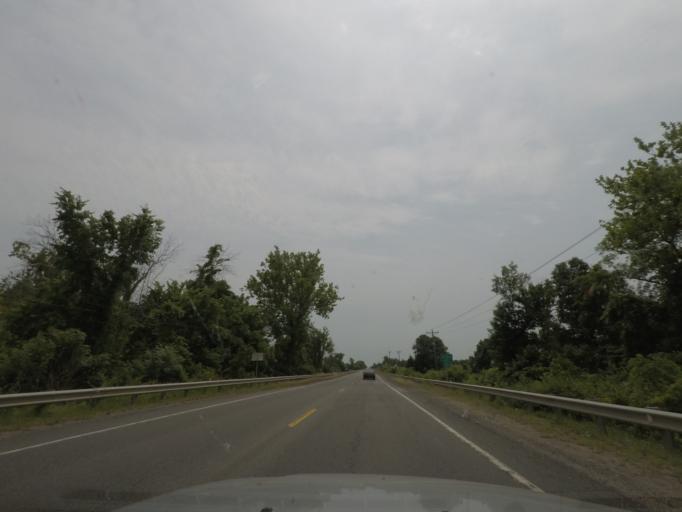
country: US
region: Virginia
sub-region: Prince William County
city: Bull Run Mountain Estates
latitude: 38.9322
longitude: -77.6250
